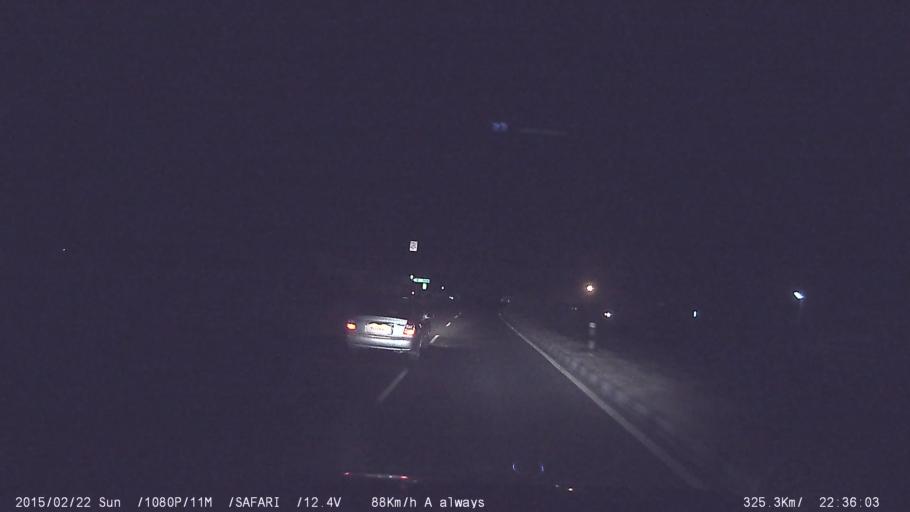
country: IN
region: Tamil Nadu
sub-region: Namakkal
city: Velur
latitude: 11.1413
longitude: 78.0208
